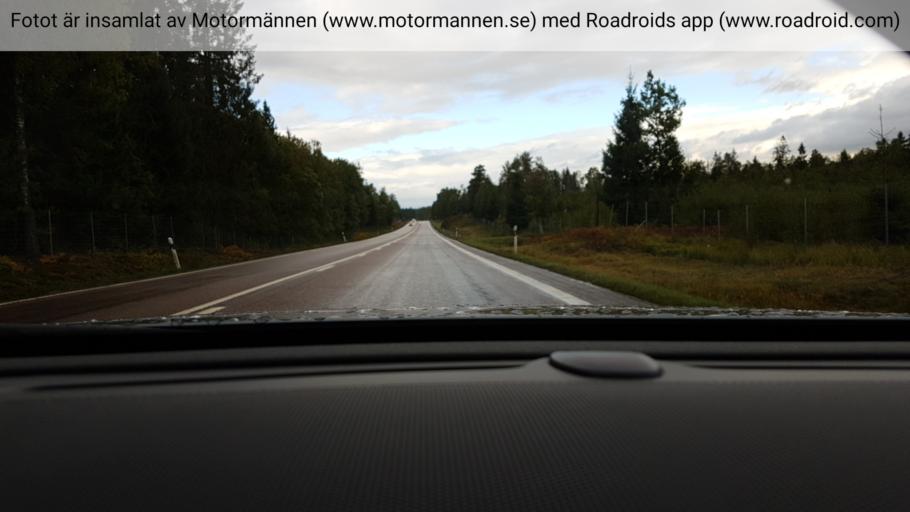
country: SE
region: Vaestra Goetaland
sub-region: Vanersborgs Kommun
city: Vanersborg
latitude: 58.4120
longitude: 12.2934
